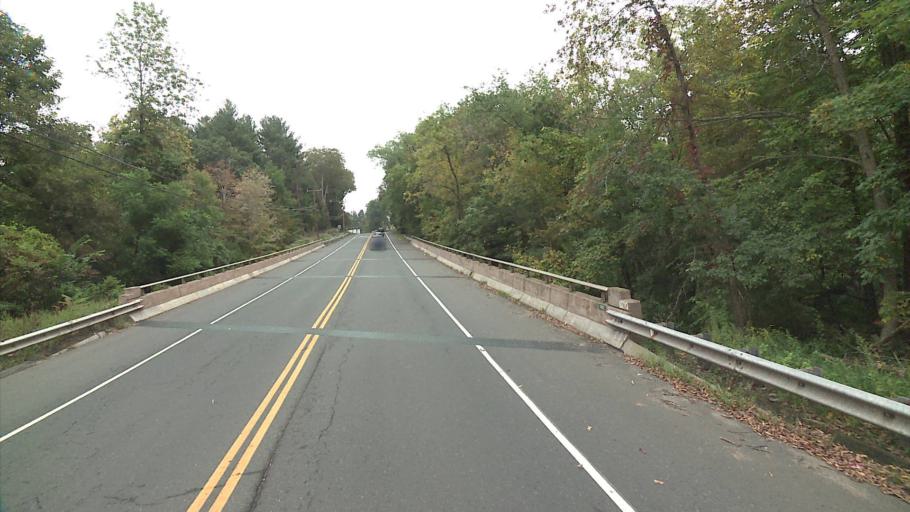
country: US
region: Connecticut
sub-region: Hartford County
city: Suffield Depot
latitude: 41.9729
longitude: -72.6576
